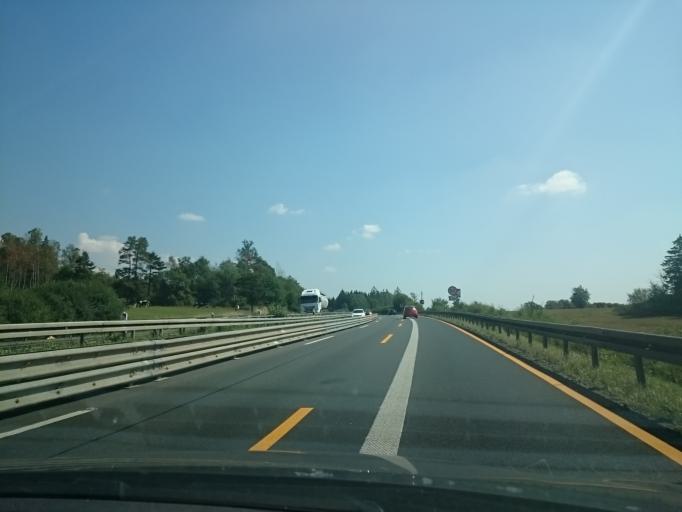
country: DE
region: Bavaria
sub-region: Upper Franconia
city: Trogen
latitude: 50.3969
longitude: 12.0046
